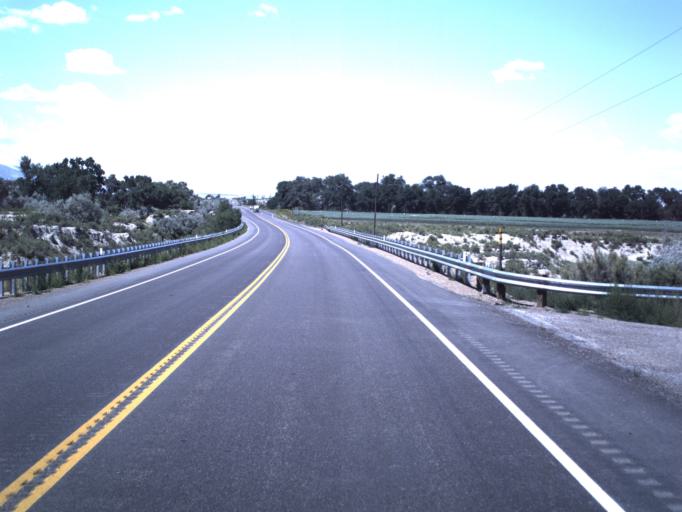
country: US
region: Utah
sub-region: Emery County
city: Huntington
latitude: 39.3003
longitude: -110.9643
